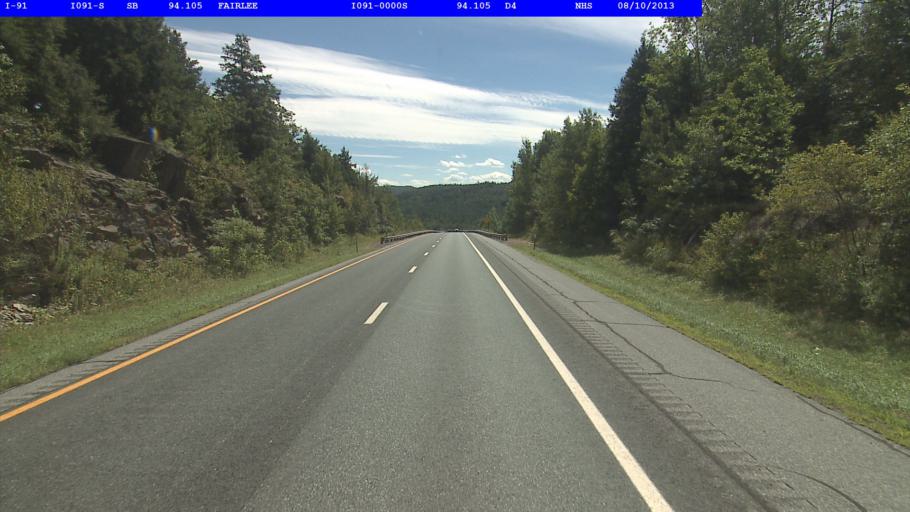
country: US
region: New Hampshire
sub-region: Grafton County
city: Orford
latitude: 43.9348
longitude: -72.1342
